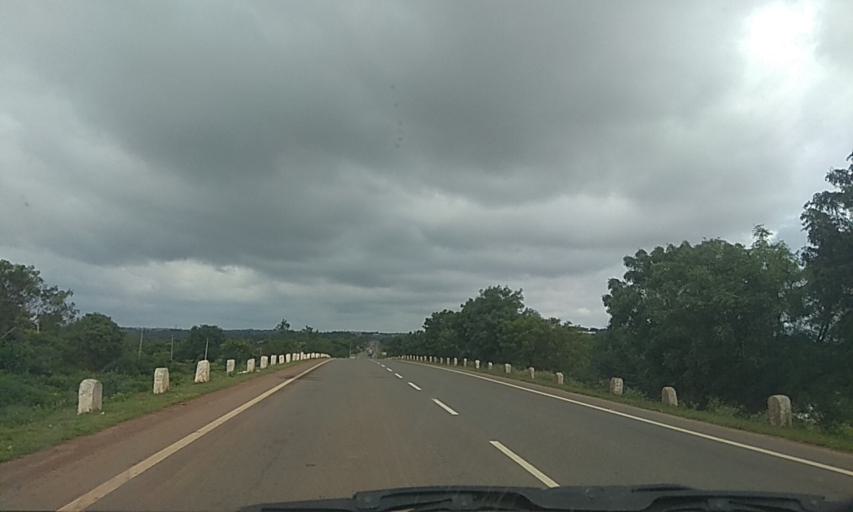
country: IN
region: Karnataka
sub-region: Dharwad
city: Hubli
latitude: 15.3424
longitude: 75.0799
